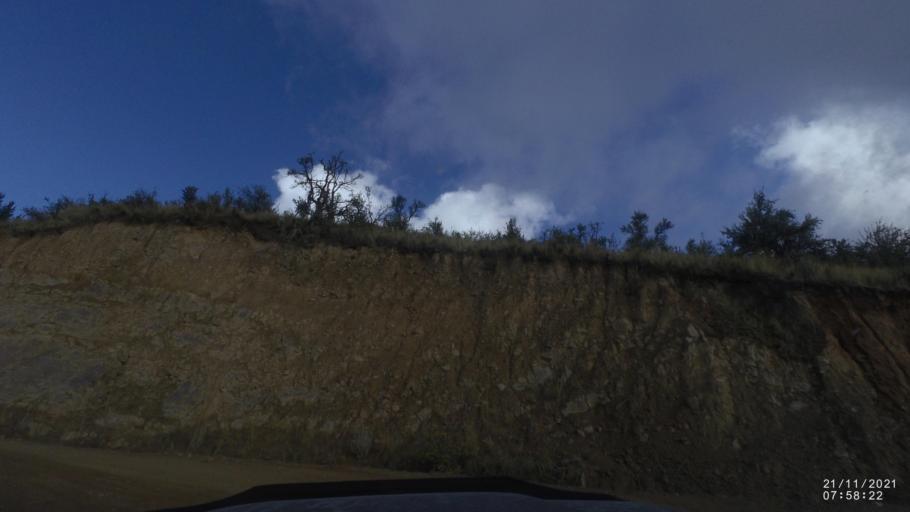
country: BO
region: Cochabamba
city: Cochabamba
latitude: -17.2943
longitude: -66.2192
